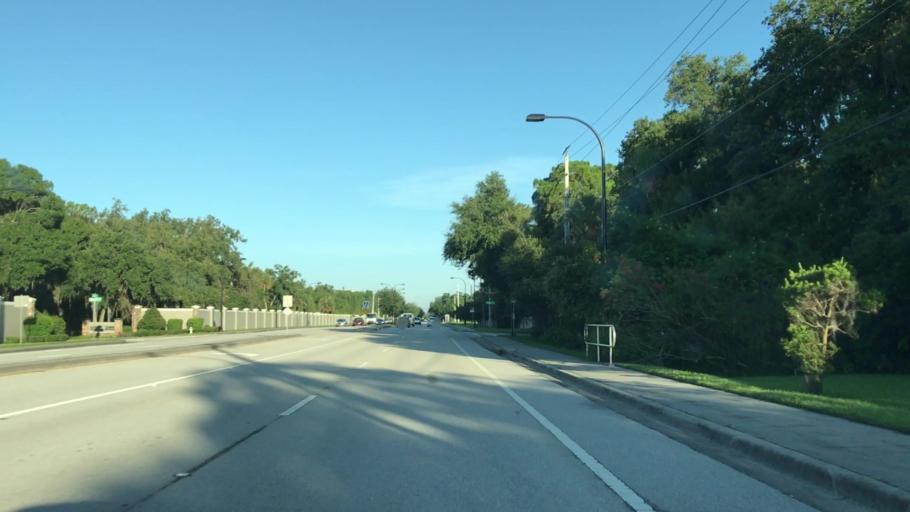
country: US
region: Florida
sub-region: Sarasota County
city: Fruitville
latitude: 27.3231
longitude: -82.4691
